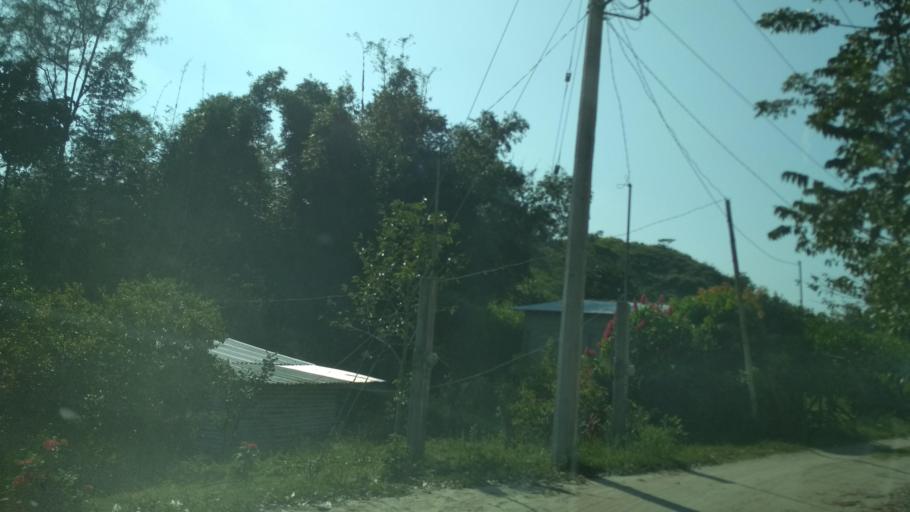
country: MX
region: Puebla
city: San Jose Acateno
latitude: 20.1800
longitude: -97.2564
